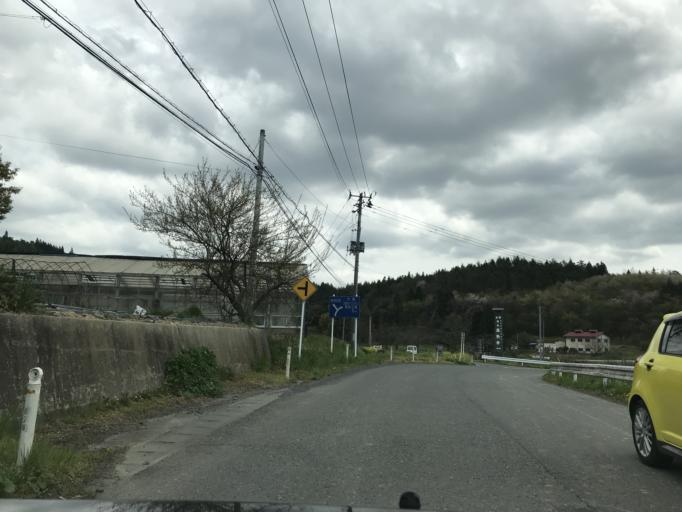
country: JP
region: Iwate
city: Ichinoseki
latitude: 38.8431
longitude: 141.3503
